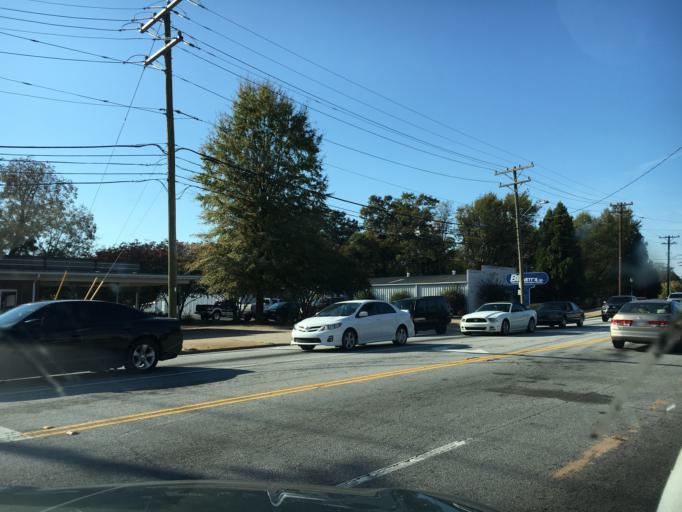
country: US
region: South Carolina
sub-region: Spartanburg County
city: Spartanburg
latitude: 34.9543
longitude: -81.9346
